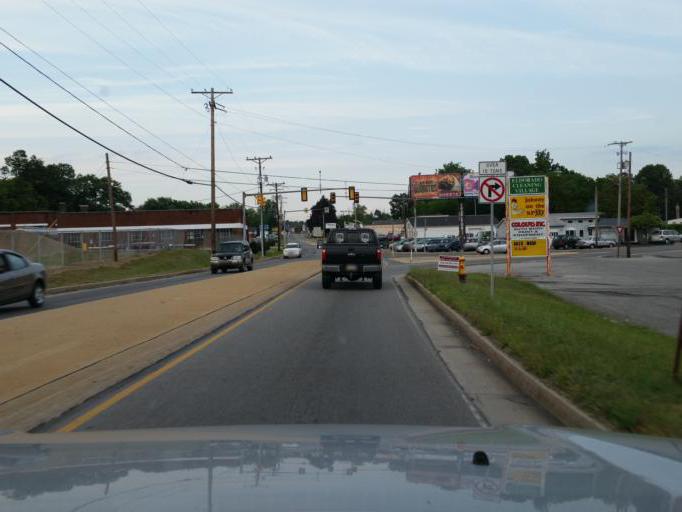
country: US
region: Pennsylvania
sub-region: Blair County
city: Lakemont
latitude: 40.4646
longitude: -78.4270
